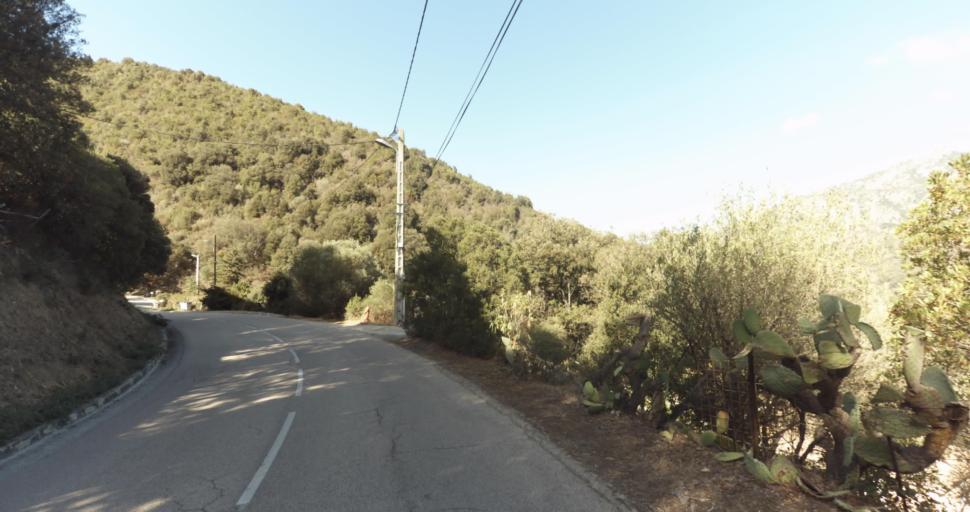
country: FR
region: Corsica
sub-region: Departement de la Corse-du-Sud
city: Ajaccio
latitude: 41.9271
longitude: 8.7077
